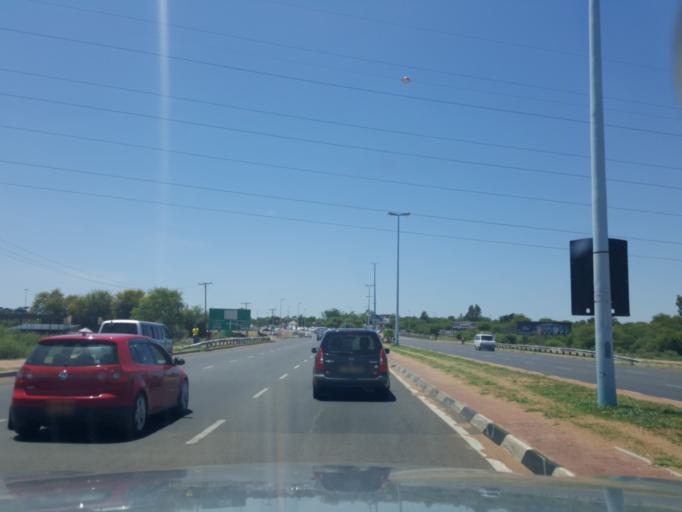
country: BW
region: Kweneng
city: Mogoditshane
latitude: -24.6433
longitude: 25.8827
